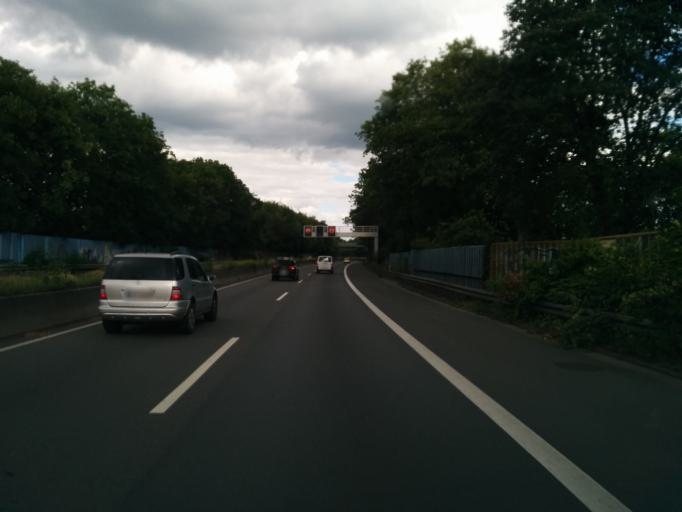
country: DE
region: North Rhine-Westphalia
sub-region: Regierungsbezirk Arnsberg
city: Bochum
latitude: 51.4985
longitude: 7.2193
